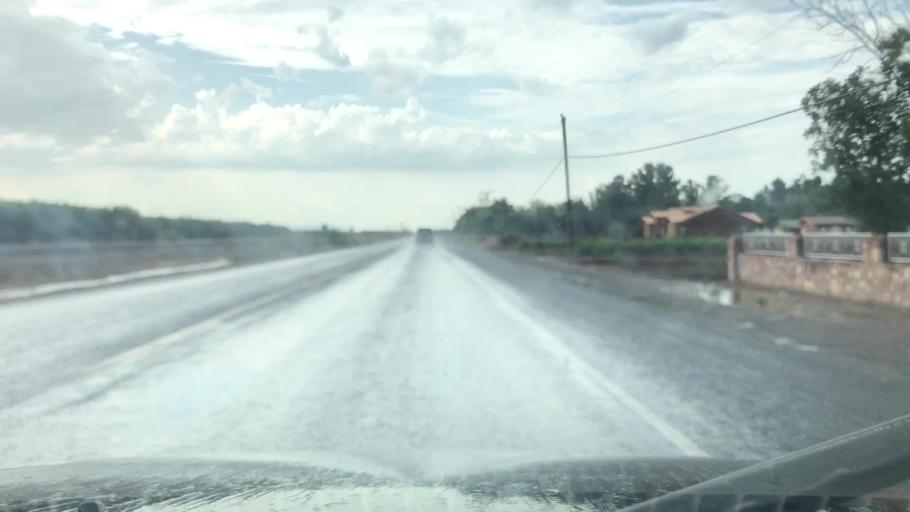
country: US
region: New Mexico
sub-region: Dona Ana County
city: Mesquite
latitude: 32.1801
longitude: -106.7063
